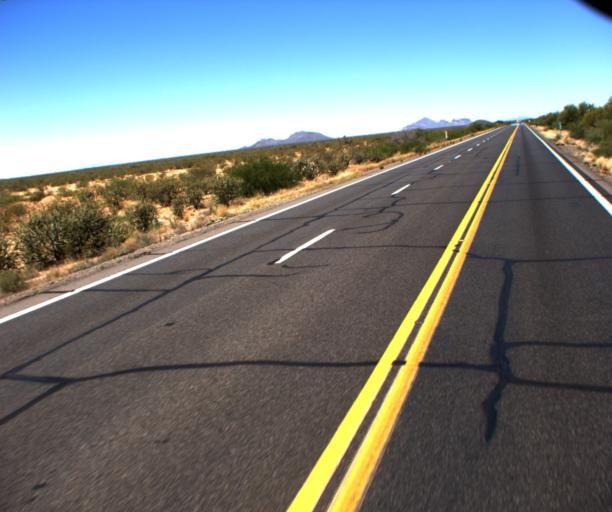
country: US
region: Arizona
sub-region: Yavapai County
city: Congress
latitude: 34.1499
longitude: -112.9886
